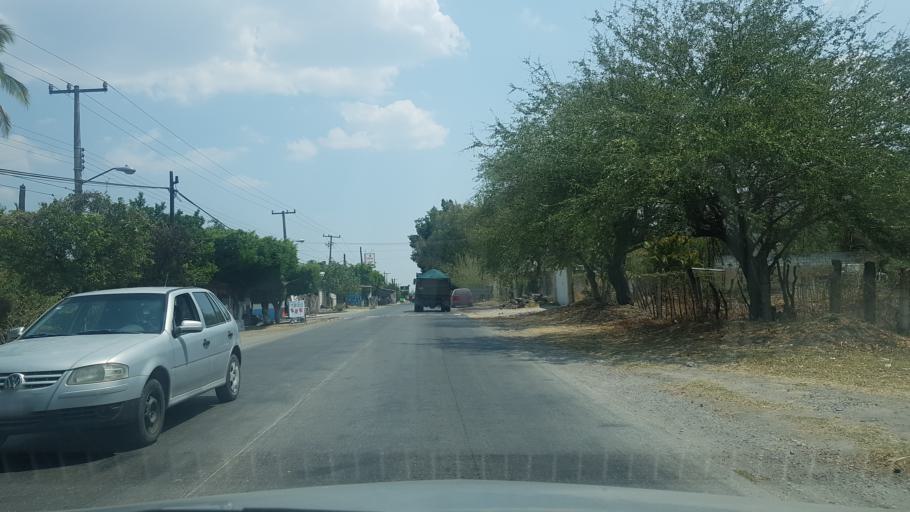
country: MX
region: Morelos
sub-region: Tlaltizapan de Zapata
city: Colonia Palo Prieto (Chipitongo)
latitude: 18.7229
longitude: -99.1219
